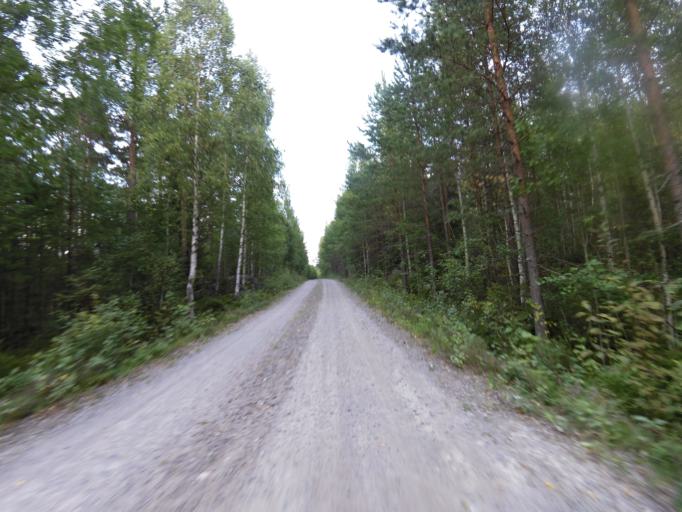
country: SE
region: Gaevleborg
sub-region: Gavle Kommun
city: Gavle
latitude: 60.7071
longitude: 17.1343
